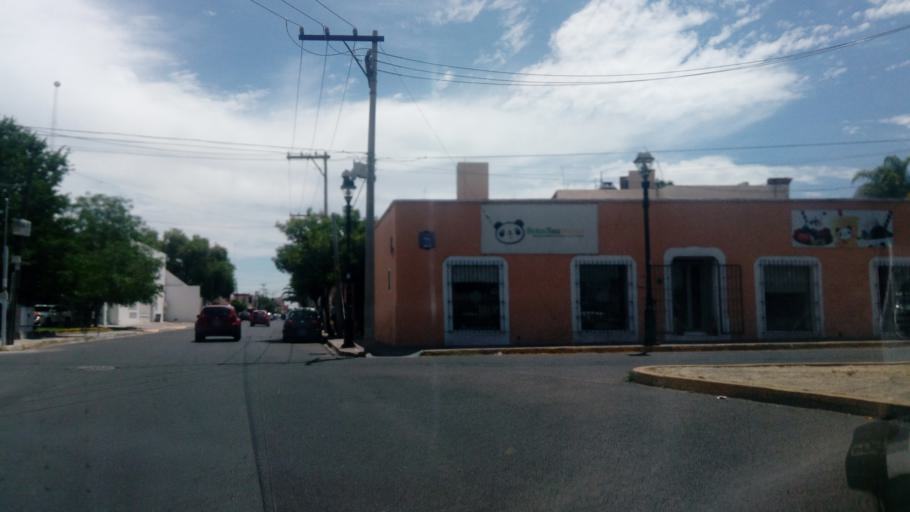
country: MX
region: Durango
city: Victoria de Durango
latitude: 24.0250
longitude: -104.6767
